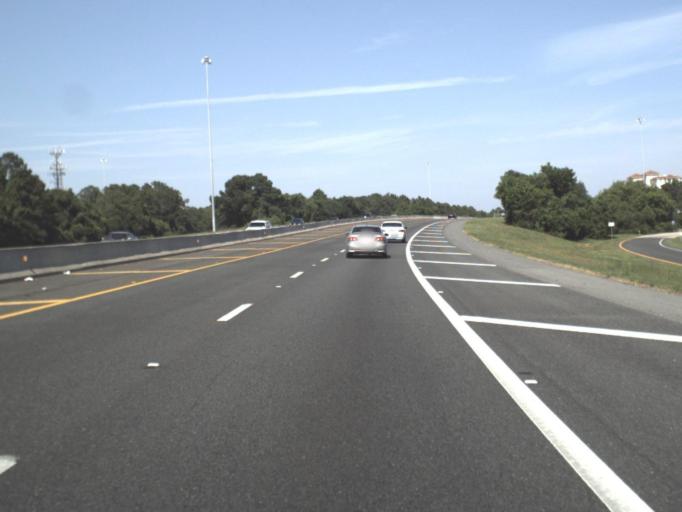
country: US
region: Florida
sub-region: Saint Johns County
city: Ponte Vedra Beach
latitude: 30.2568
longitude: -81.4407
